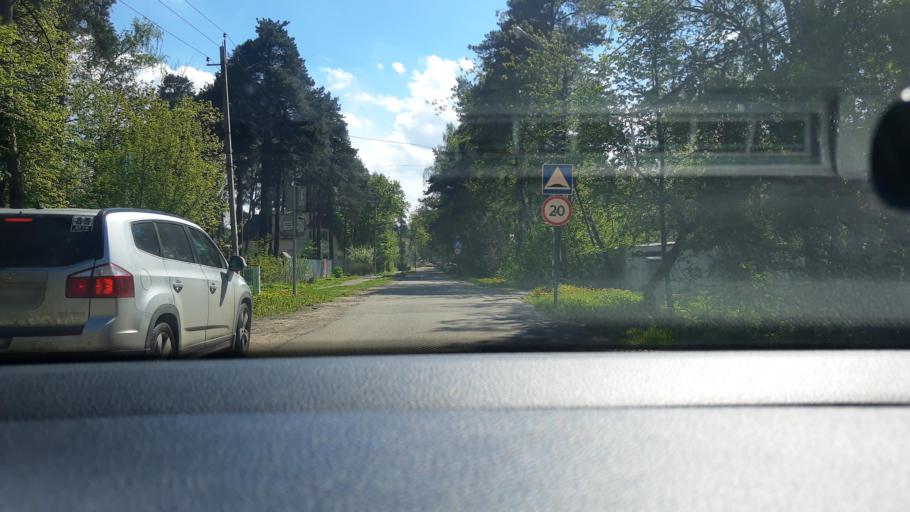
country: RU
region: Moskovskaya
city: Druzhba
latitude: 55.8999
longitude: 37.7474
